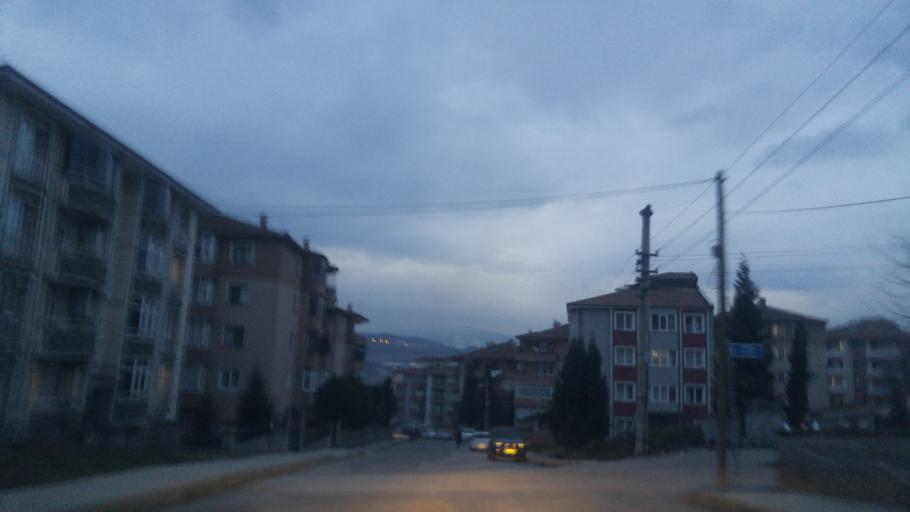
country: TR
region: Karabuk
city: Karabuk
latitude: 41.2201
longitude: 32.6646
